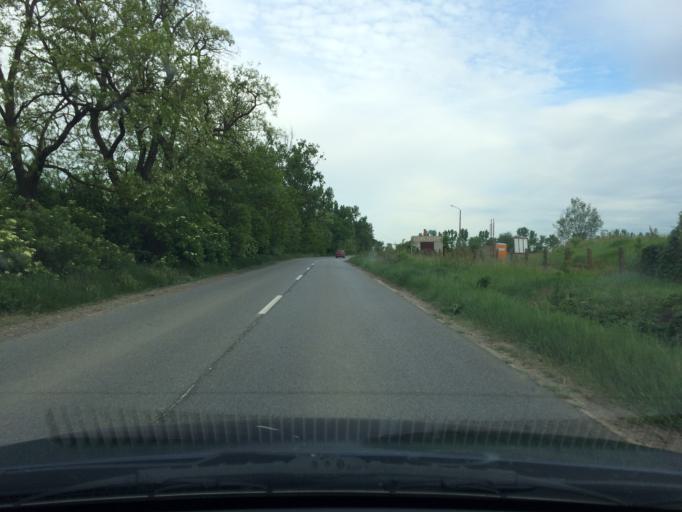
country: HU
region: Szabolcs-Szatmar-Bereg
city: Tiszavasvari
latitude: 47.9365
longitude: 21.3824
